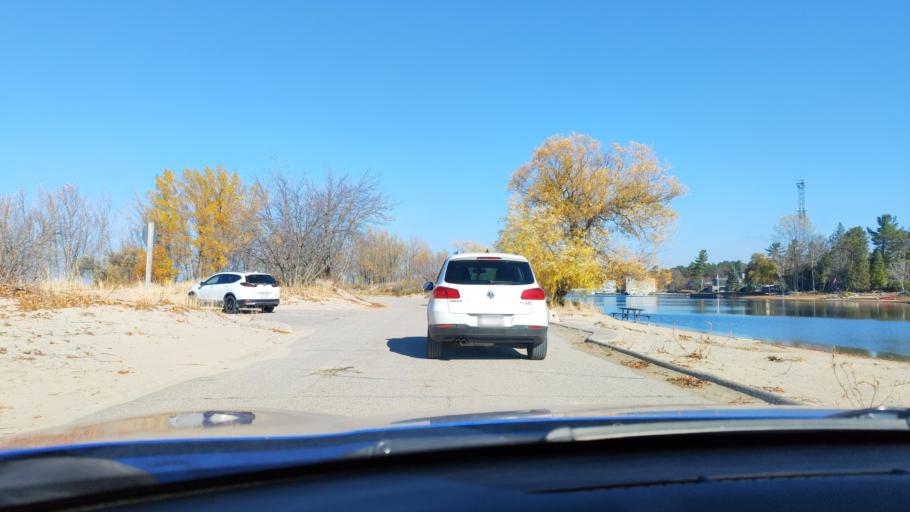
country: CA
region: Ontario
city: Wasaga Beach
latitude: 44.5312
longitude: -80.0120
